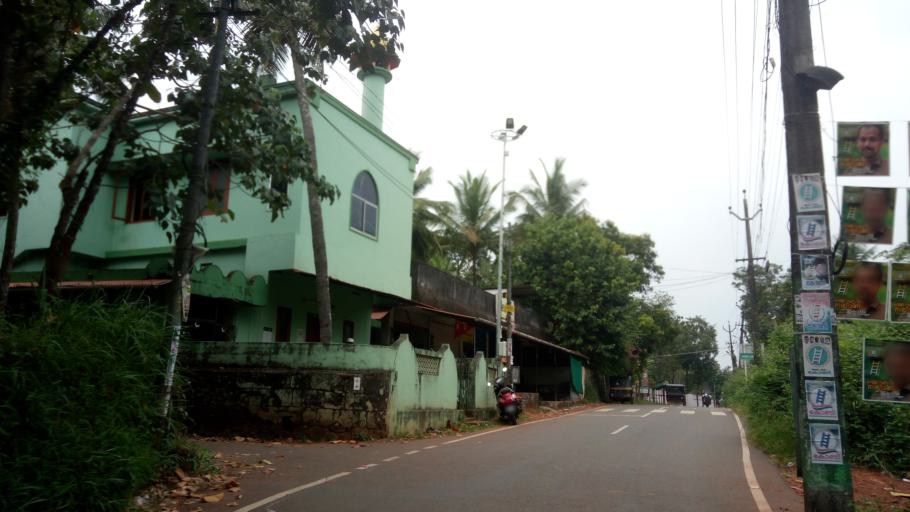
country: IN
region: Kerala
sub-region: Malappuram
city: Malappuram
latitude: 10.9817
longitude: 76.0064
